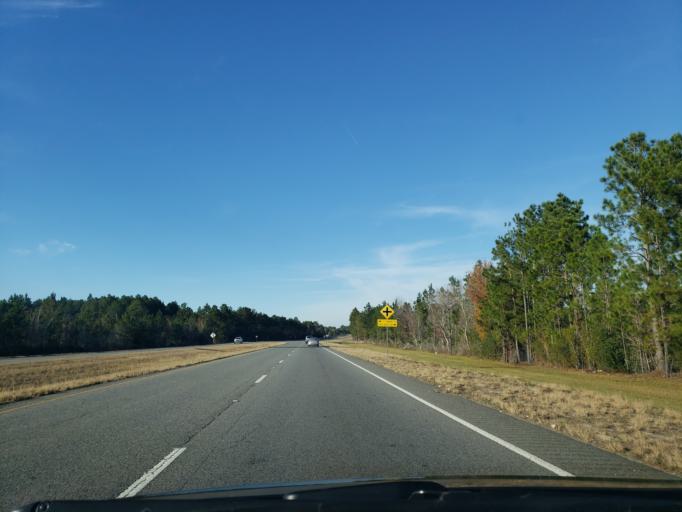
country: US
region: Georgia
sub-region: Ware County
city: Deenwood
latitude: 31.2260
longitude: -82.4254
